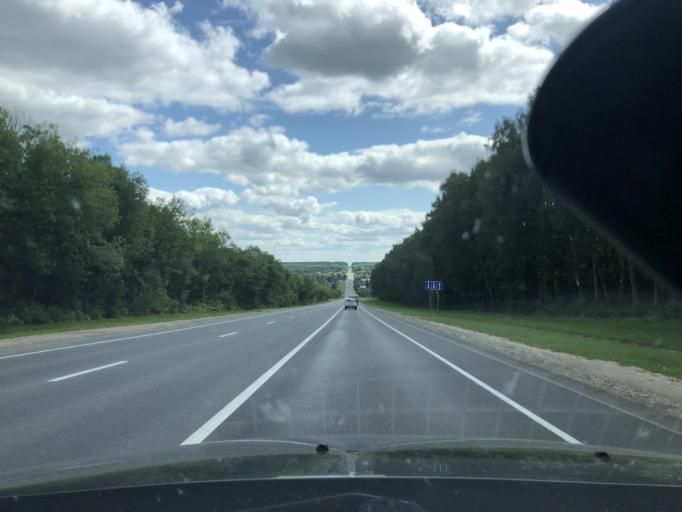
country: RU
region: Tula
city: Gorelki
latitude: 54.3123
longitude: 37.5661
